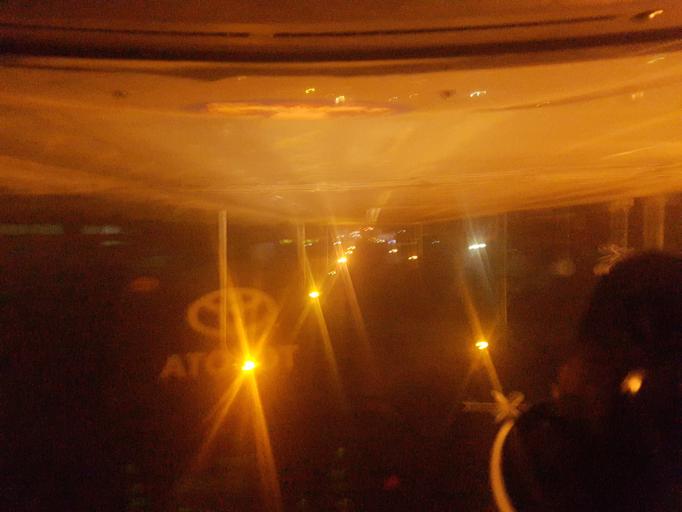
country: MN
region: Ulaanbaatar
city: Ulaanbaatar
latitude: 47.9033
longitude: 106.8725
